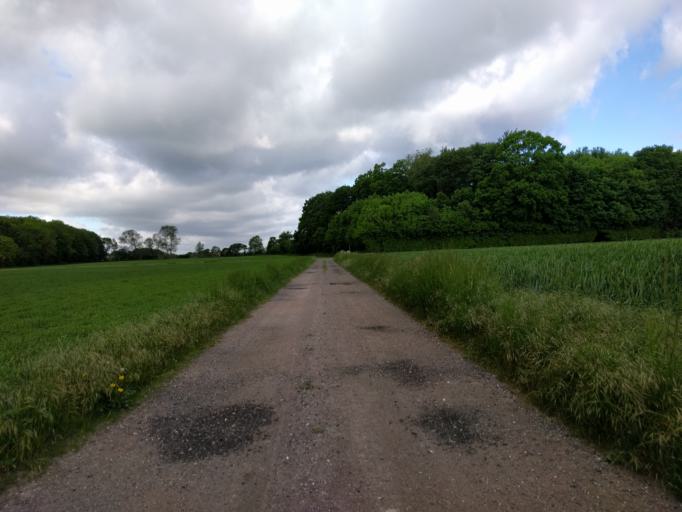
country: DK
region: South Denmark
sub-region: Kerteminde Kommune
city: Kerteminde
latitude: 55.4206
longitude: 10.6289
